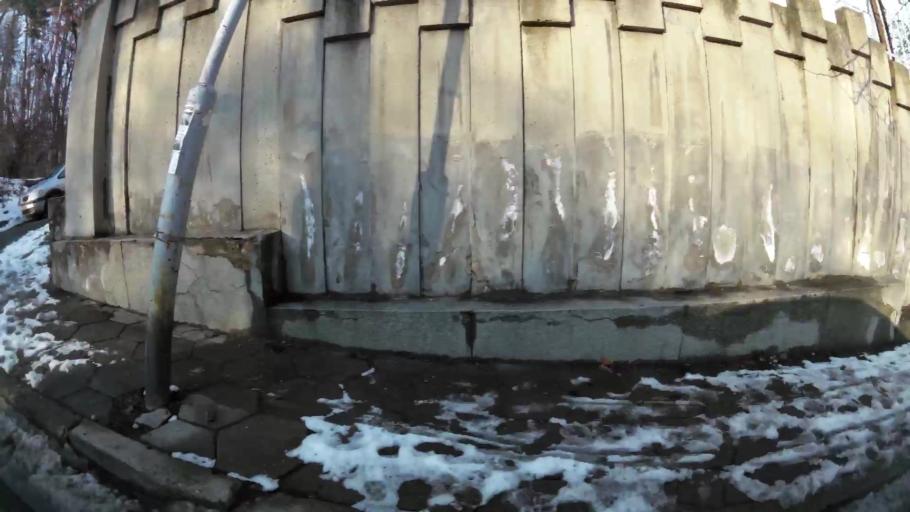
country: BG
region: Sofia-Capital
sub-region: Stolichna Obshtina
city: Sofia
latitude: 42.6701
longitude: 23.3442
